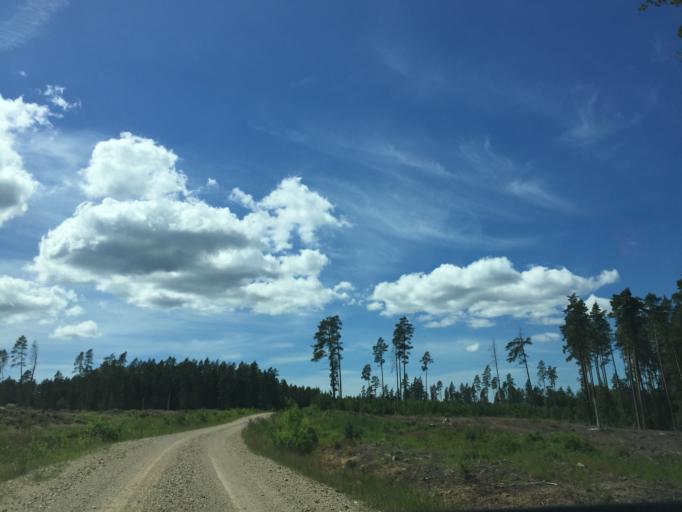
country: LV
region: Kuldigas Rajons
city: Kuldiga
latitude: 57.1098
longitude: 21.8738
